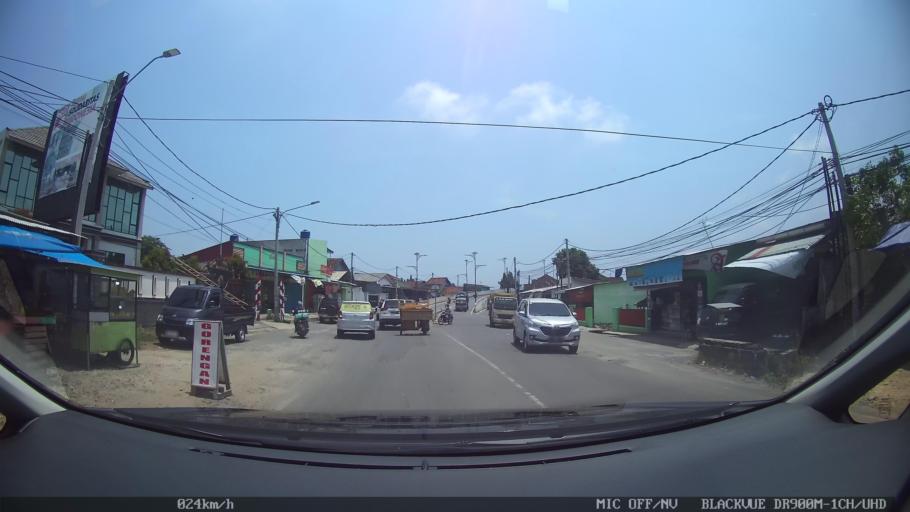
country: ID
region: Lampung
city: Kedaton
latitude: -5.3629
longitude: 105.2562
